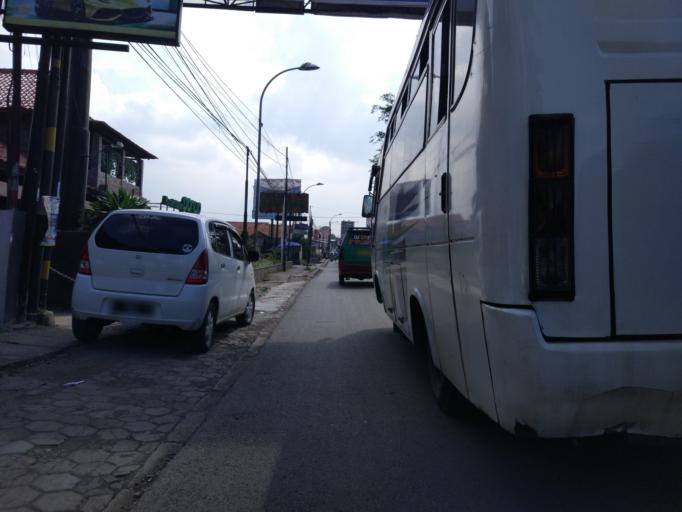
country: ID
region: West Java
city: Cileunyi
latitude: -6.9366
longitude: 107.7296
